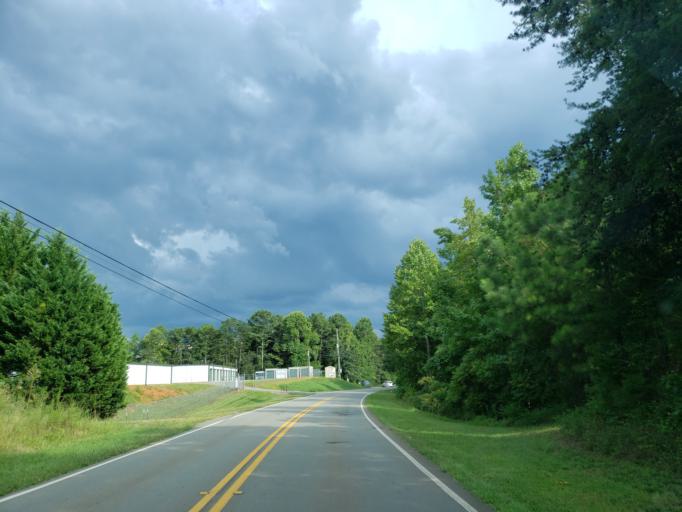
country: US
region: Georgia
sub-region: Pickens County
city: Jasper
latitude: 34.4072
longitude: -84.4812
